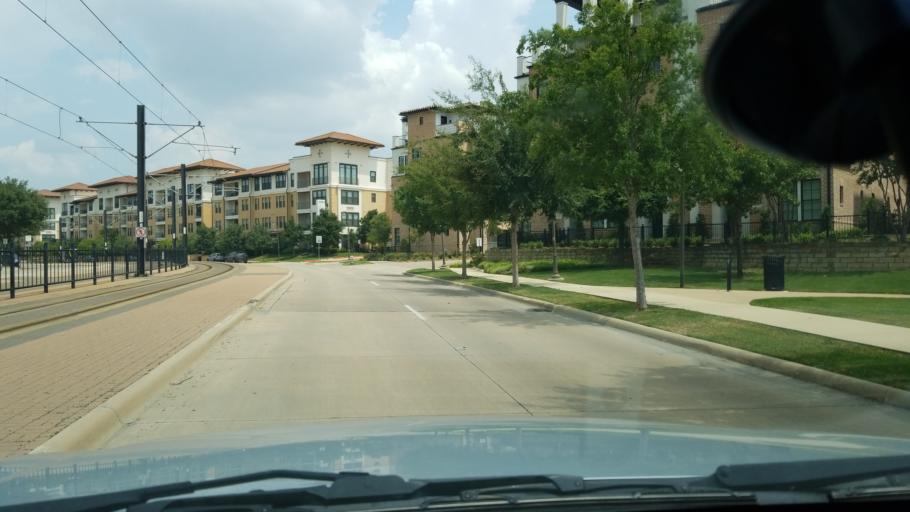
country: US
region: Texas
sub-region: Dallas County
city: Irving
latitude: 32.8623
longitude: -96.9284
